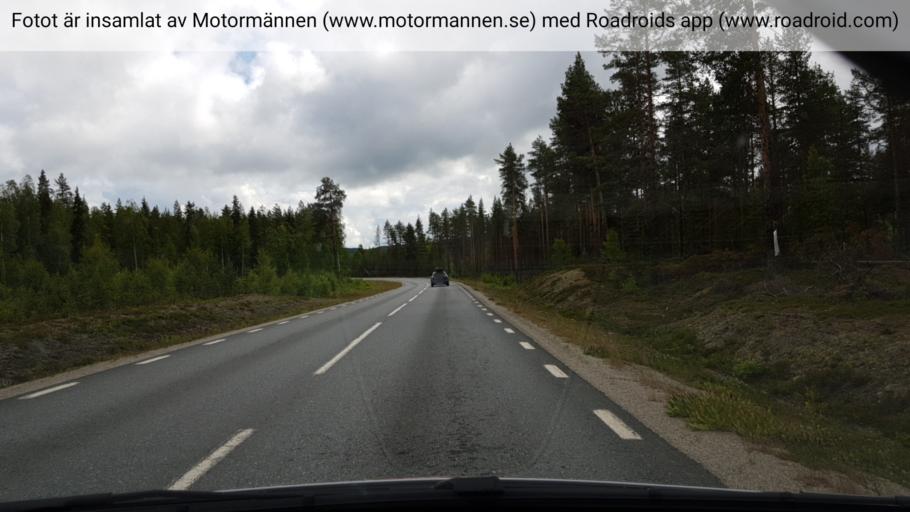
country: SE
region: Vaesterbotten
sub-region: Lycksele Kommun
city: Lycksele
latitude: 64.4100
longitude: 19.0214
